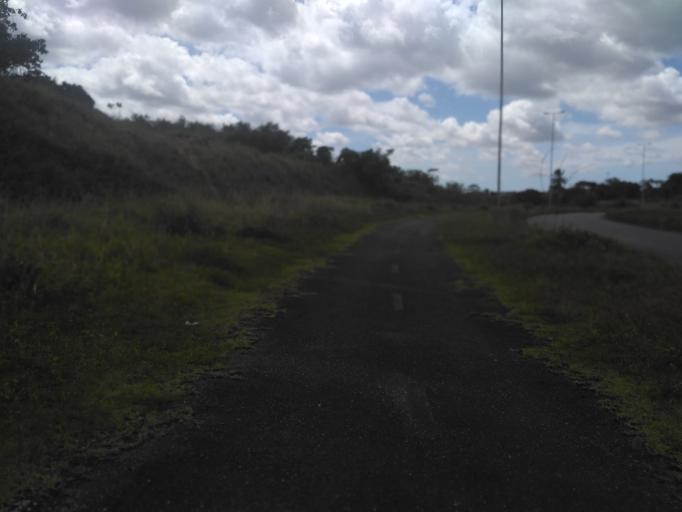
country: BR
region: Pernambuco
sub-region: Sao Lourenco Da Mata
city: Sao Lourenco da Mata
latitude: -8.0404
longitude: -35.0040
